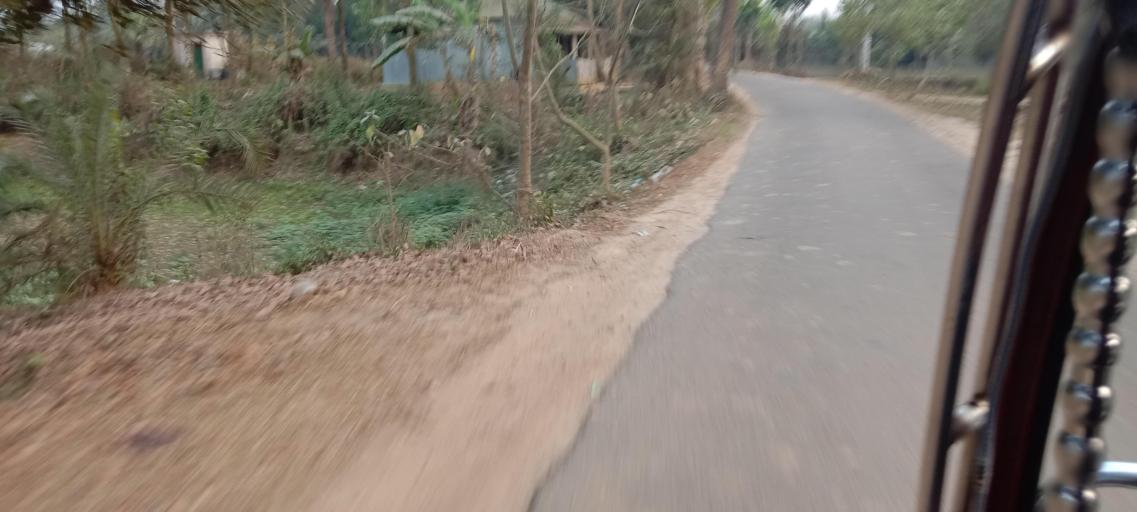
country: BD
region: Dhaka
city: Sakhipur
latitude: 24.4333
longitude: 90.2629
